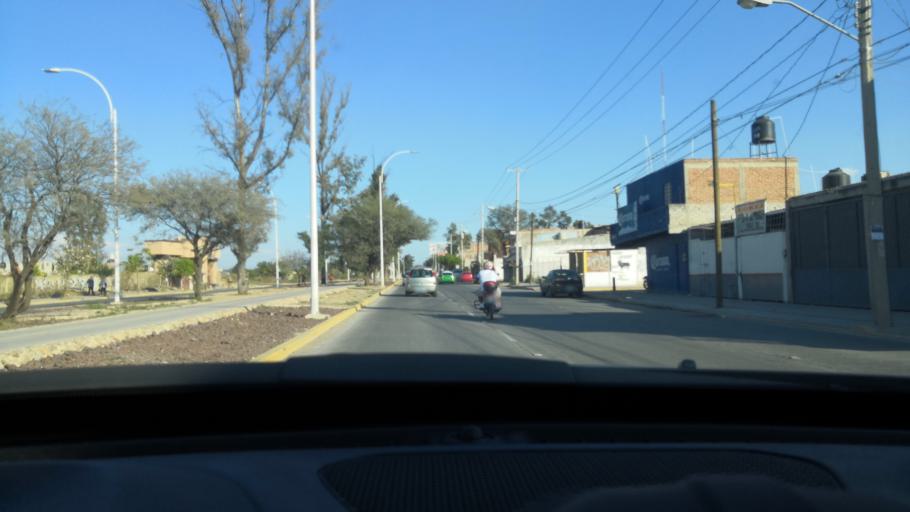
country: MX
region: Guanajuato
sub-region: Leon
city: San Jose de Duran (Los Troncoso)
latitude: 21.0610
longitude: -101.6164
